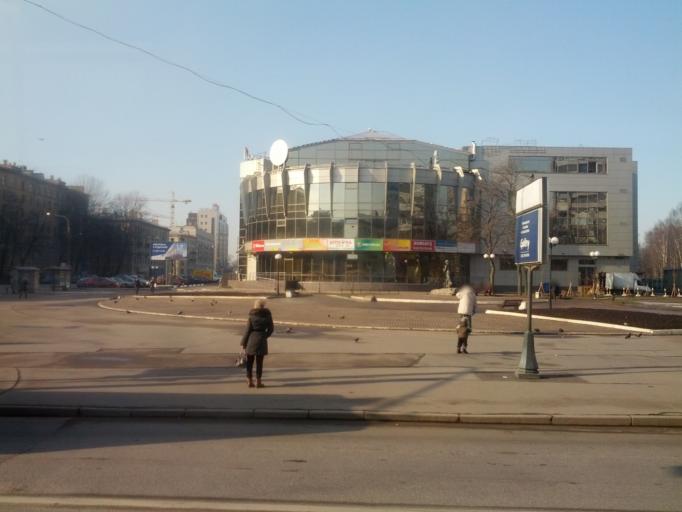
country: RU
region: Leningrad
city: Kalininskiy
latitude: 59.9597
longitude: 30.4153
